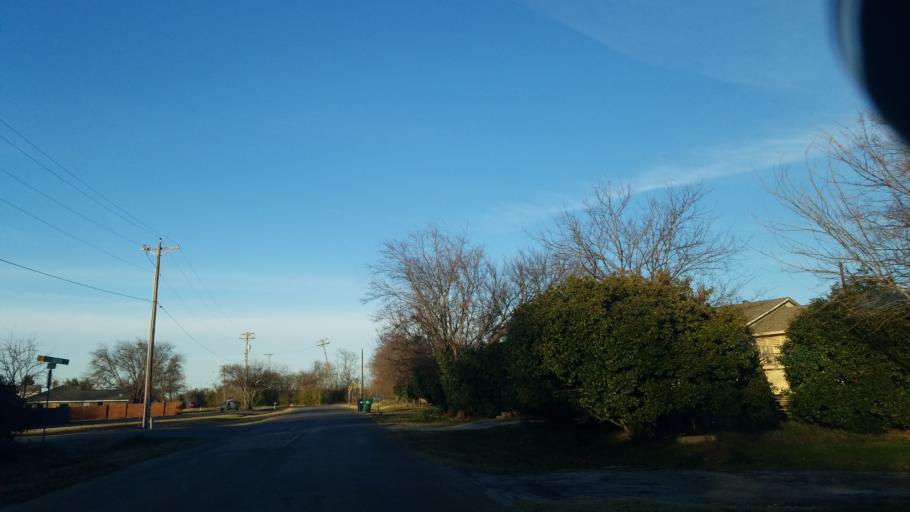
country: US
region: Texas
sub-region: Denton County
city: Denton
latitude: 33.1878
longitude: -97.1622
